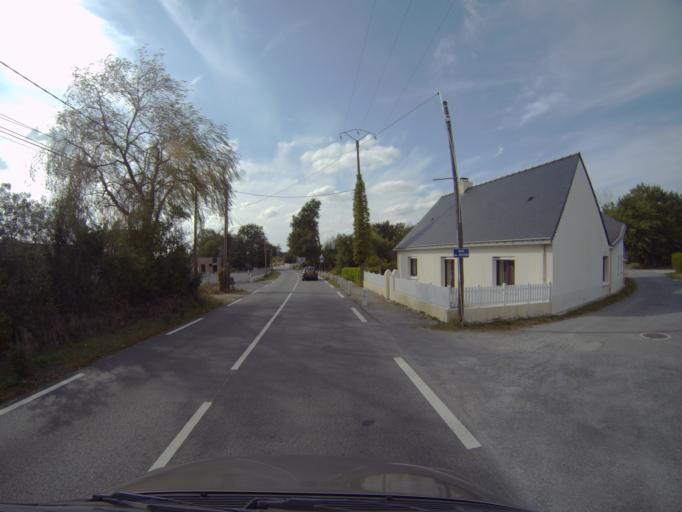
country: FR
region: Pays de la Loire
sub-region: Departement de la Loire-Atlantique
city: Sautron
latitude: 47.2448
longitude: -1.6873
